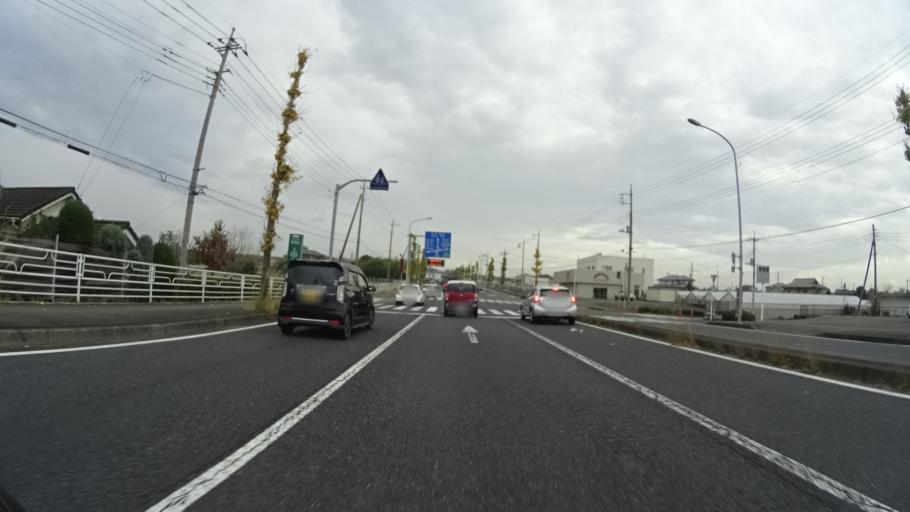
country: JP
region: Gunma
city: Isesaki
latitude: 36.3692
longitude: 139.1495
